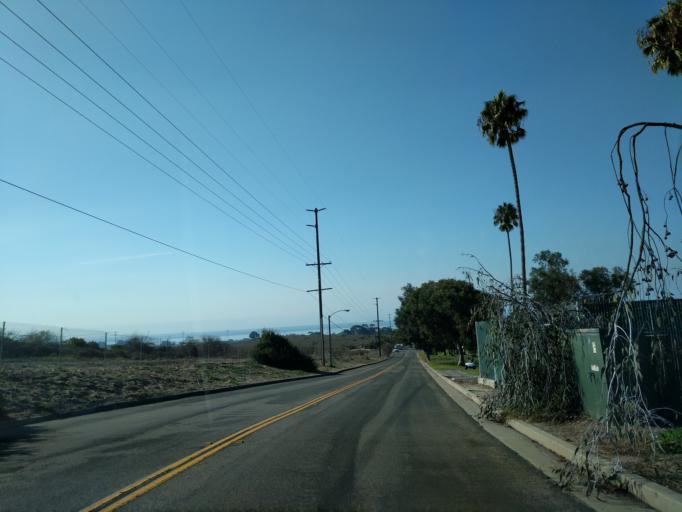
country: US
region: California
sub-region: Orange County
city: San Clemente
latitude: 33.4051
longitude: -117.5916
